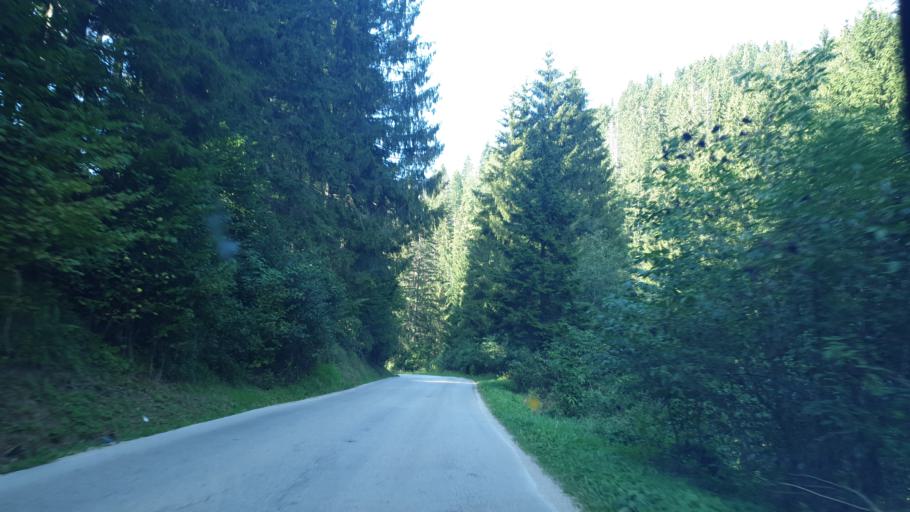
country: RS
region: Central Serbia
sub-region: Zlatiborski Okrug
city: Nova Varos
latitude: 43.4548
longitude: 19.8418
